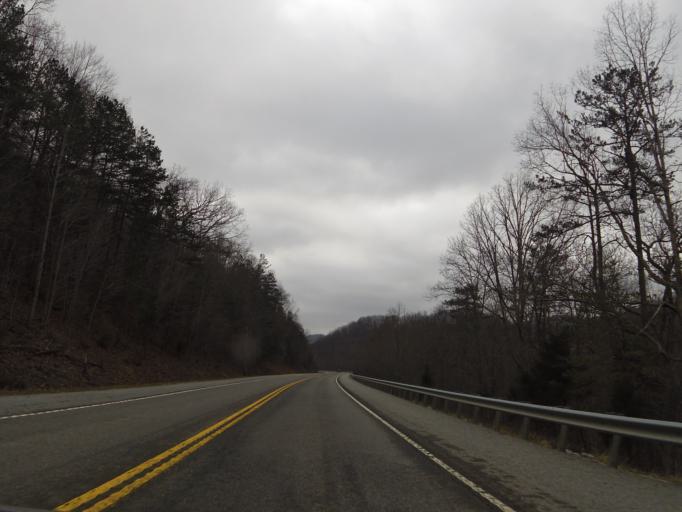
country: US
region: Tennessee
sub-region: Campbell County
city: Caryville
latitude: 36.4105
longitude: -84.2960
